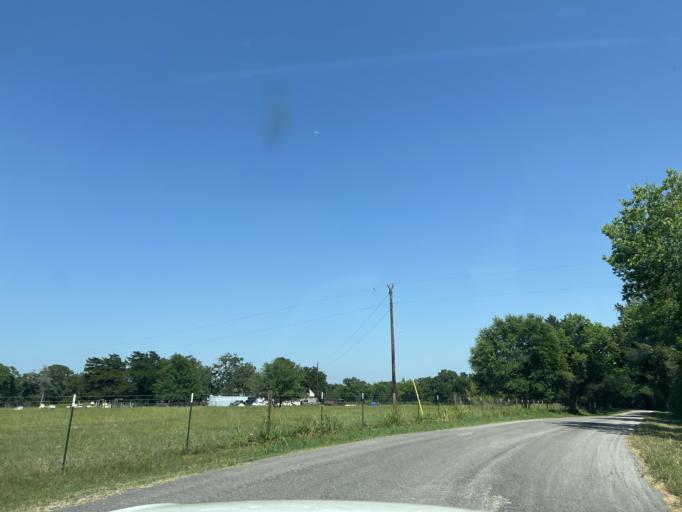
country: US
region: Texas
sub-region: Washington County
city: Brenham
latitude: 30.1729
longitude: -96.5027
